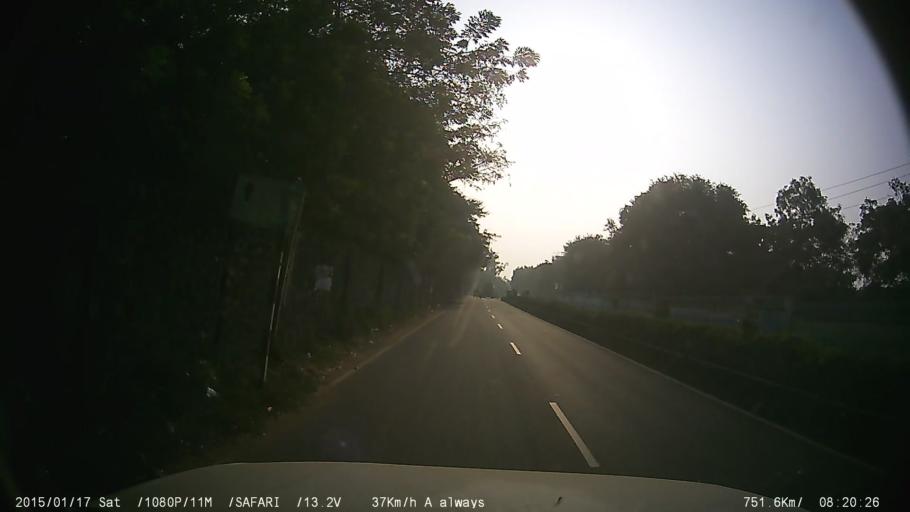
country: IN
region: Tamil Nadu
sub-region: Kancheepuram
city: Vandalur
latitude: 12.8781
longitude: 80.0834
